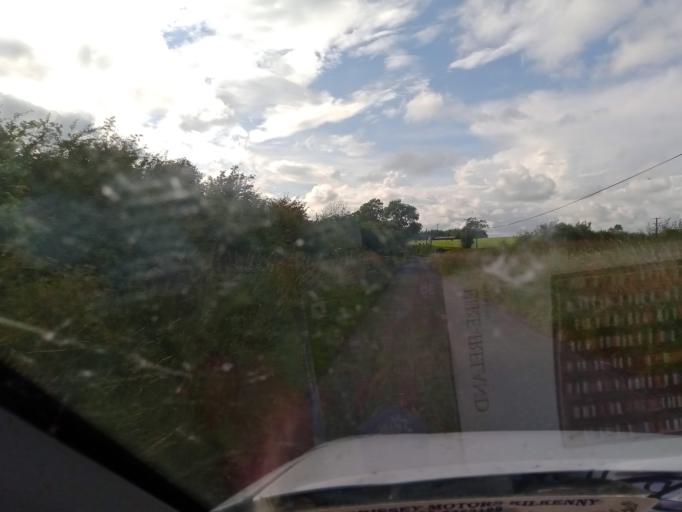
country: IE
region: Leinster
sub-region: Laois
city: Rathdowney
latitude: 52.7884
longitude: -7.5547
